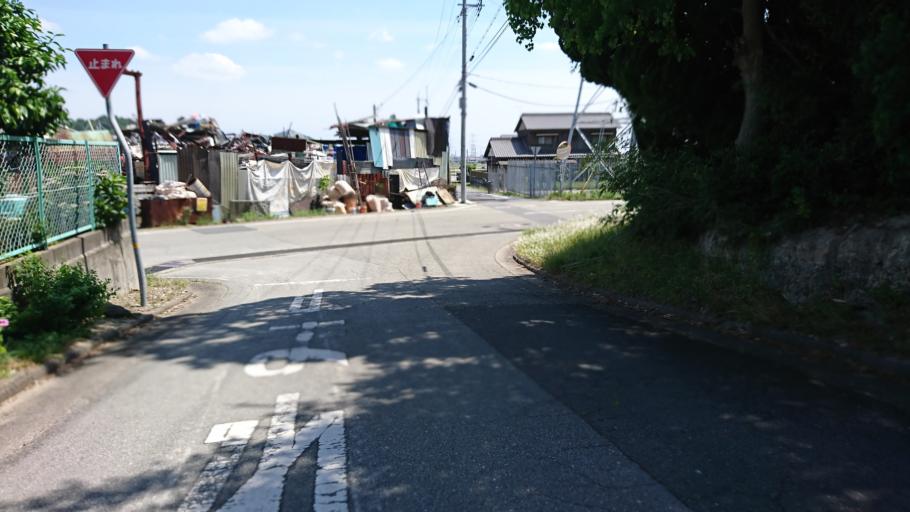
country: JP
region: Hyogo
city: Kakogawacho-honmachi
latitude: 34.8041
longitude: 134.7858
